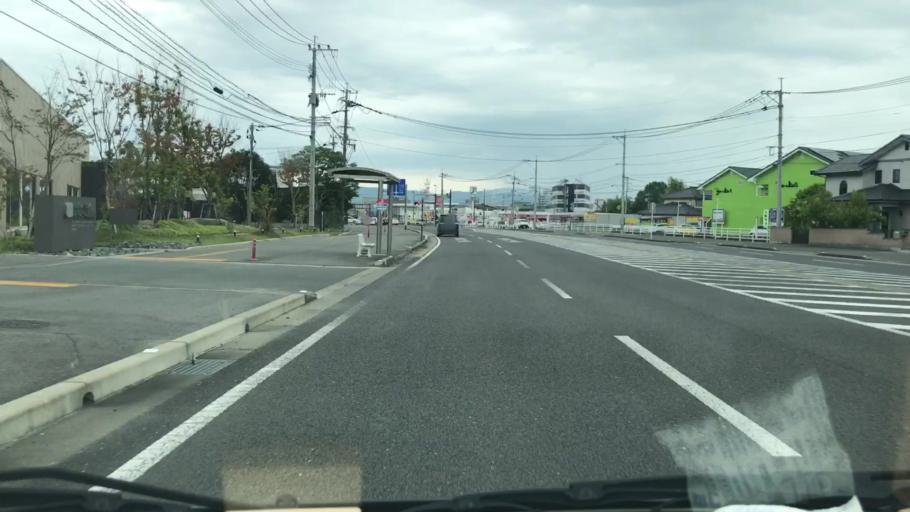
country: JP
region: Saga Prefecture
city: Saga-shi
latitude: 33.2372
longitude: 130.2941
